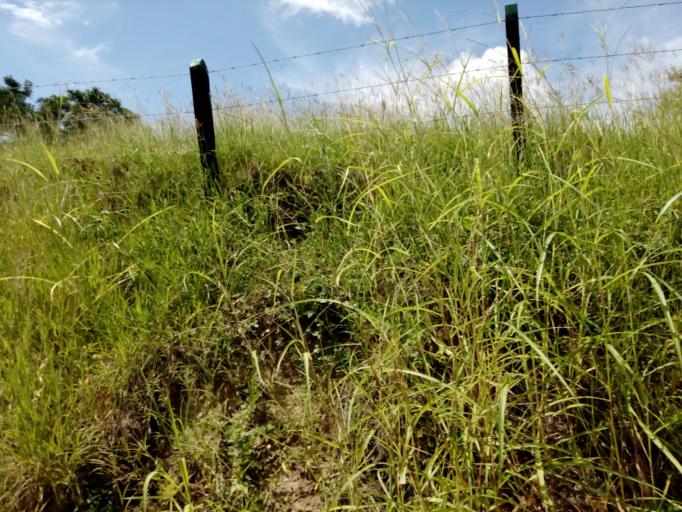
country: CO
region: Boyaca
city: Puerto Boyaca
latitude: 5.9593
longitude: -74.4585
